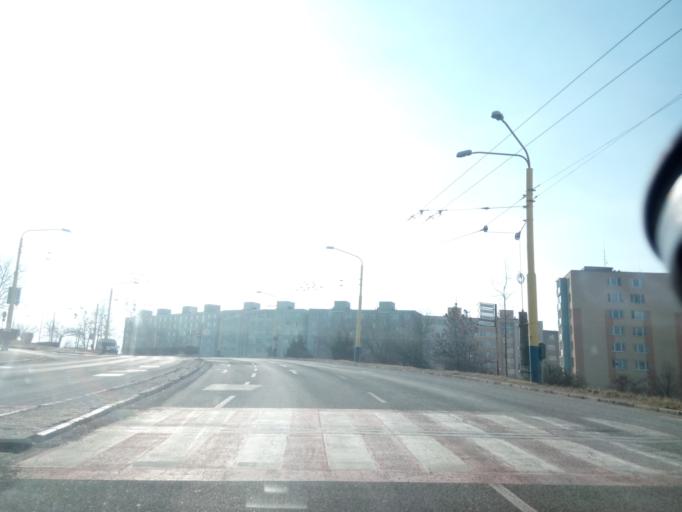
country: SK
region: Kosicky
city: Kosice
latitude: 48.7337
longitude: 21.2850
